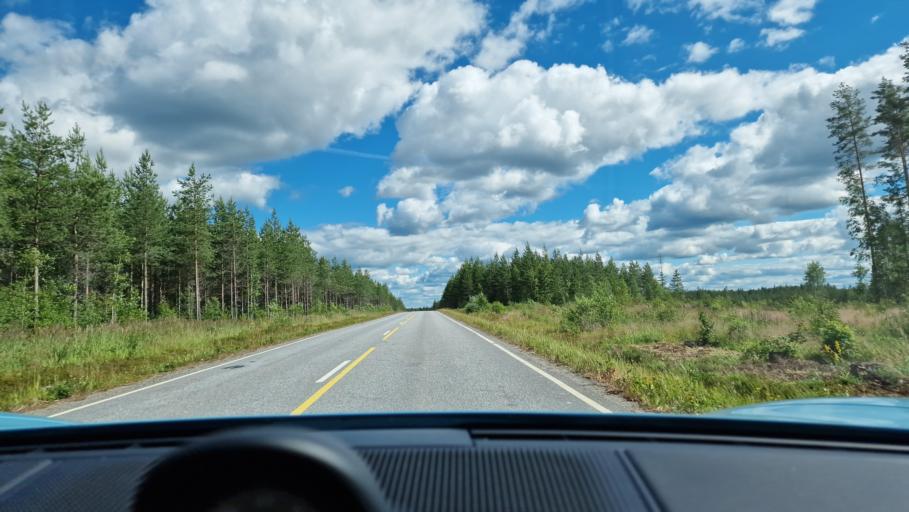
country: FI
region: Central Finland
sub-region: Saarijaervi-Viitasaari
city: Pylkoenmaeki
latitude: 62.6620
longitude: 24.5570
